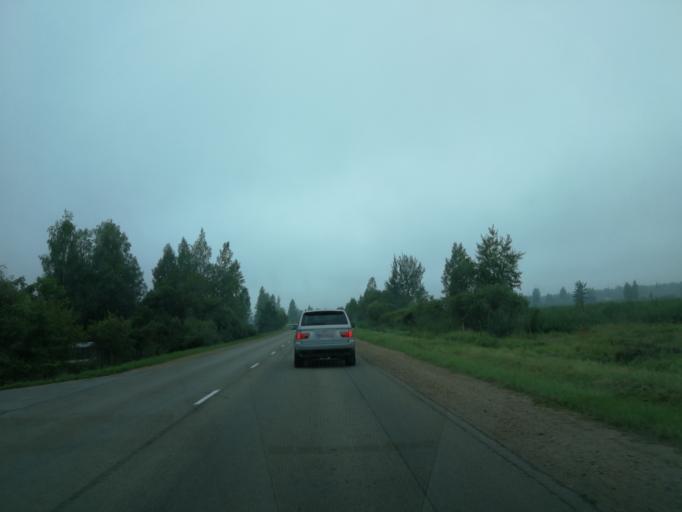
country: LV
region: Preilu Rajons
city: Preili
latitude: 56.3007
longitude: 26.7272
